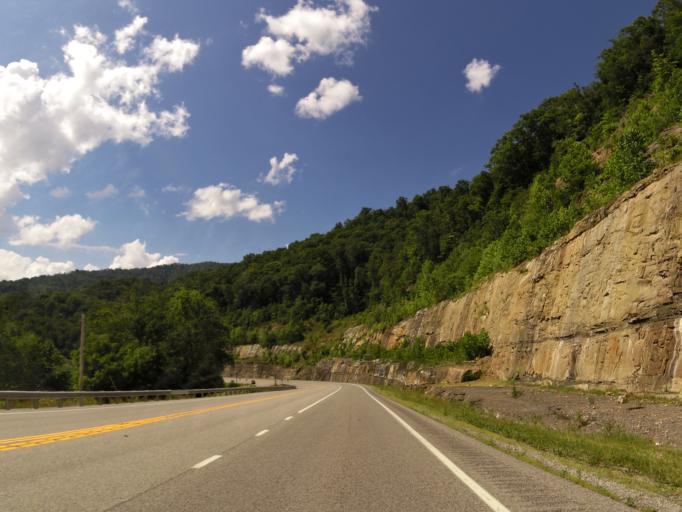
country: US
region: Kentucky
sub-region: Harlan County
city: Harlan
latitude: 36.8132
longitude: -83.2704
